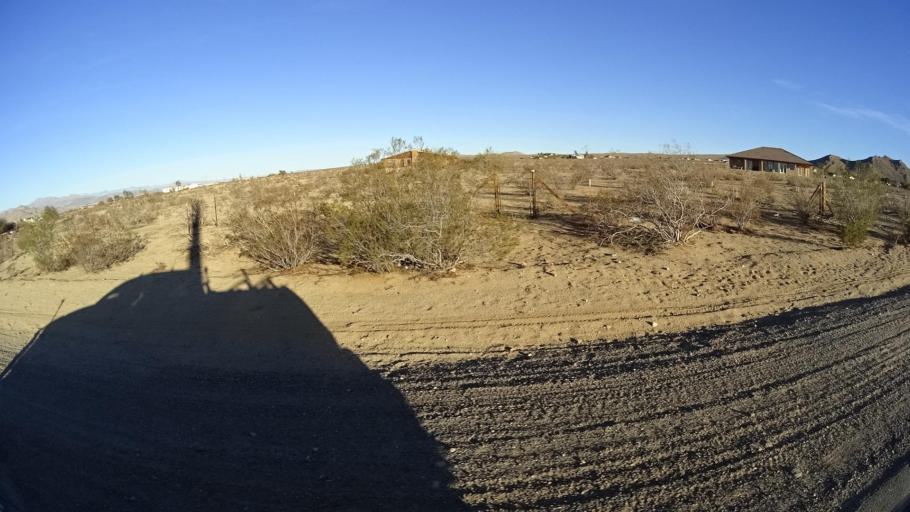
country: US
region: California
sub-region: Kern County
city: Ridgecrest
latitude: 35.5876
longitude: -117.6530
